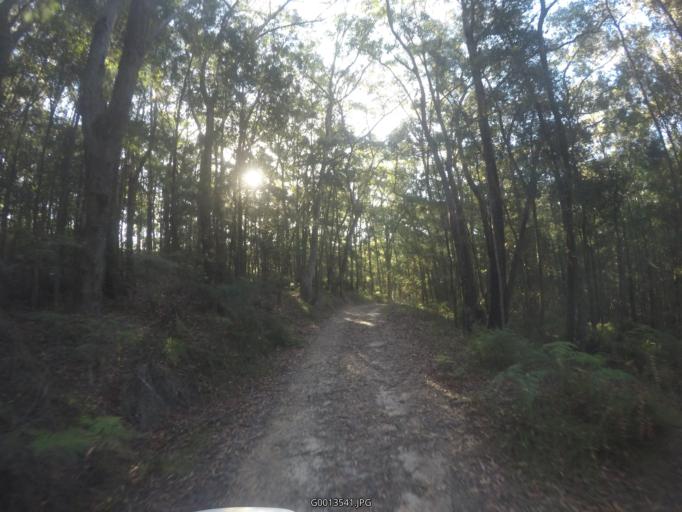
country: AU
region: New South Wales
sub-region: Lake Macquarie Shire
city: Cooranbong
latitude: -33.0856
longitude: 151.3579
